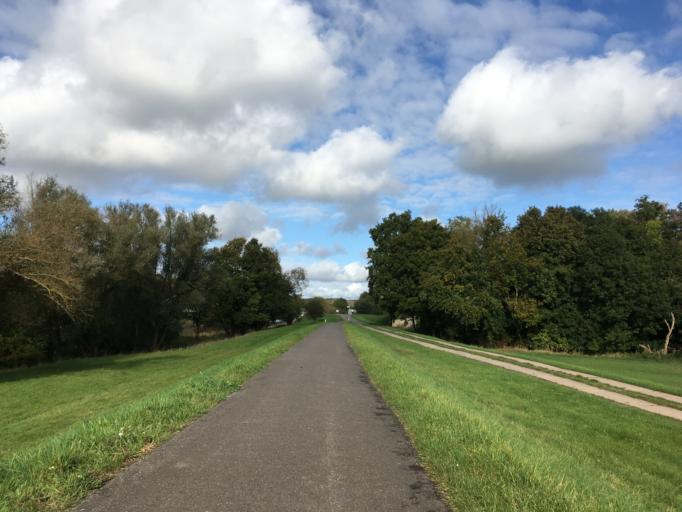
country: DE
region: Brandenburg
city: Schoneberg
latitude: 52.9480
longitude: 14.1109
